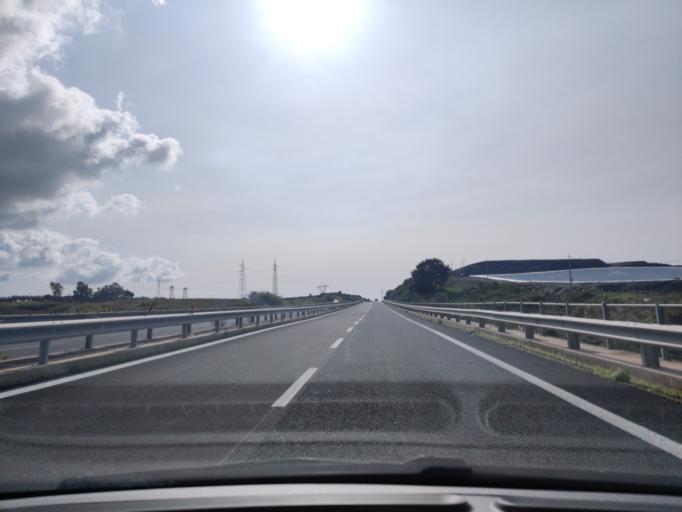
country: IT
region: Latium
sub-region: Citta metropolitana di Roma Capitale
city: Aurelia
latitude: 42.1182
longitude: 11.7913
